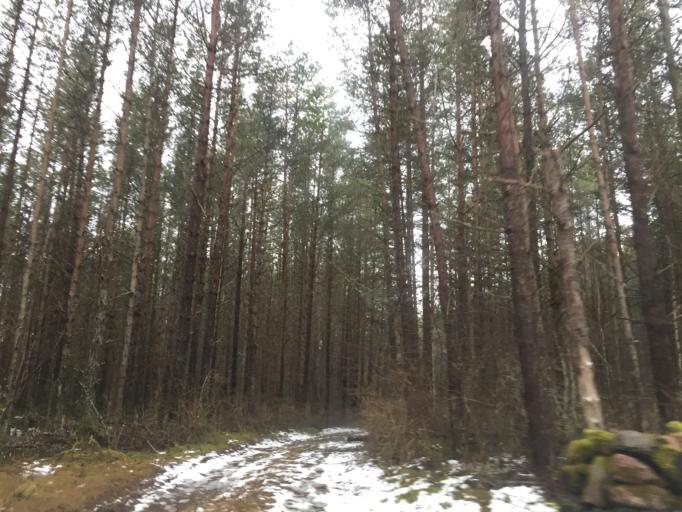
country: EE
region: Saare
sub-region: Orissaare vald
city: Orissaare
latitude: 58.6119
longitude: 22.9558
